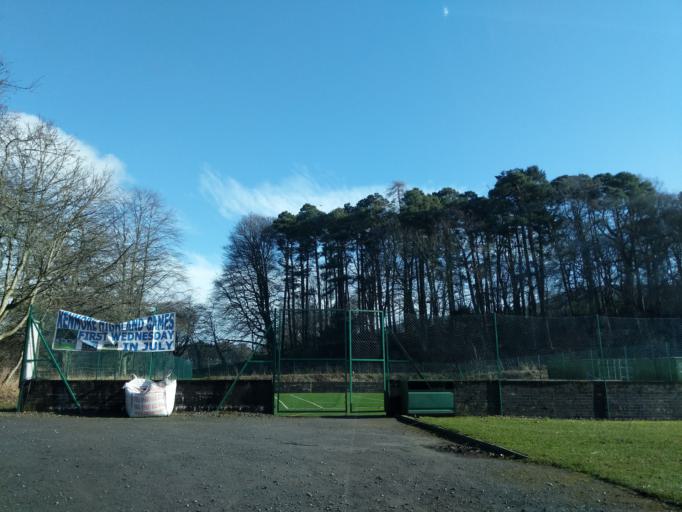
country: GB
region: Scotland
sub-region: Perth and Kinross
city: Aberfeldy
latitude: 56.5851
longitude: -3.9950
